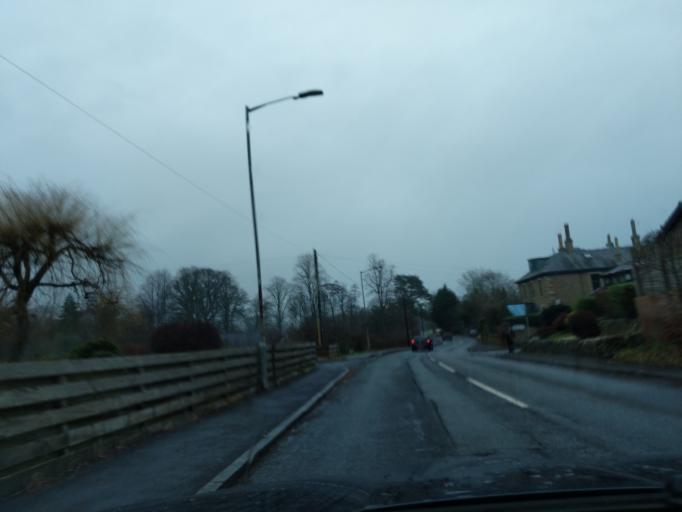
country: GB
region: Scotland
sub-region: The Scottish Borders
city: Melrose
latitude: 55.6024
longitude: -2.7404
